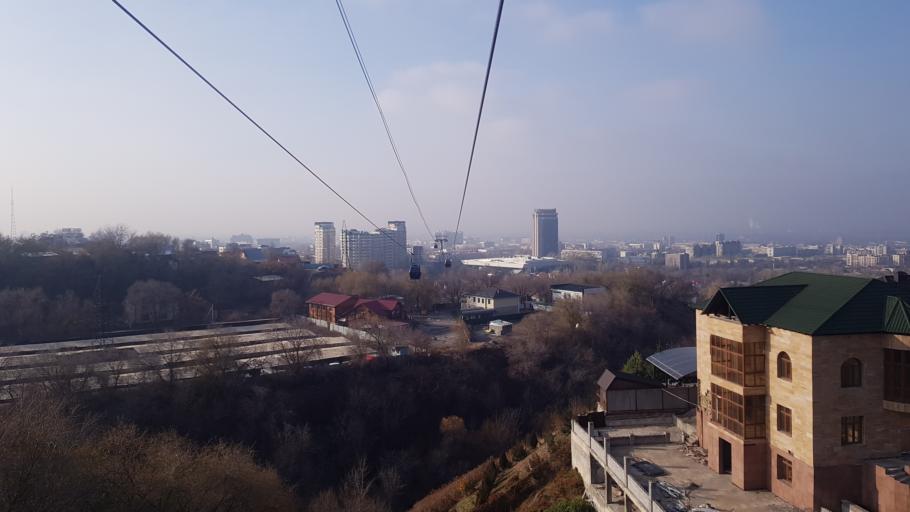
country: KZ
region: Almaty Qalasy
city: Almaty
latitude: 43.2376
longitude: 76.9688
